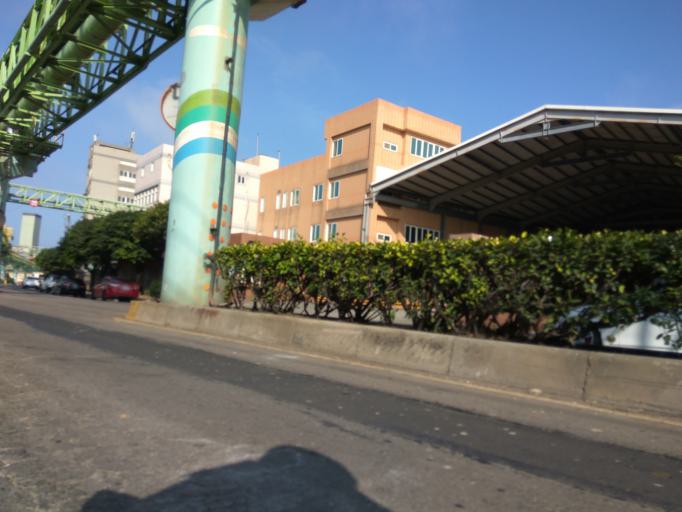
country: TW
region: Taiwan
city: Taoyuan City
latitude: 25.0766
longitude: 121.1757
